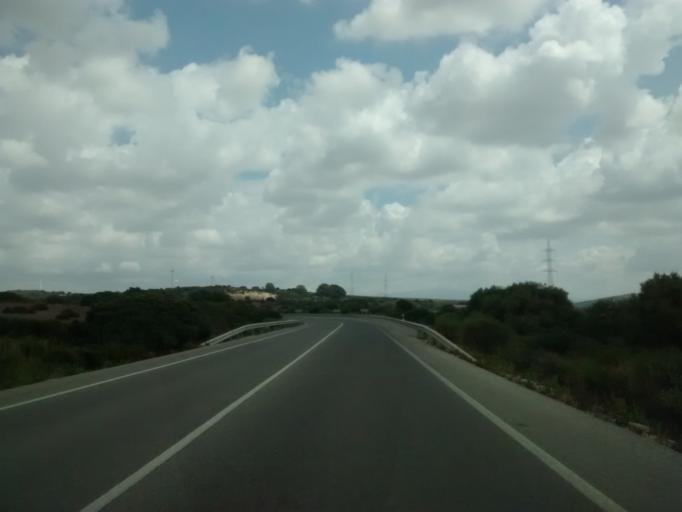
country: ES
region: Andalusia
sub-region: Provincia de Cadiz
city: Medina Sidonia
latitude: 36.4451
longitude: -5.8933
